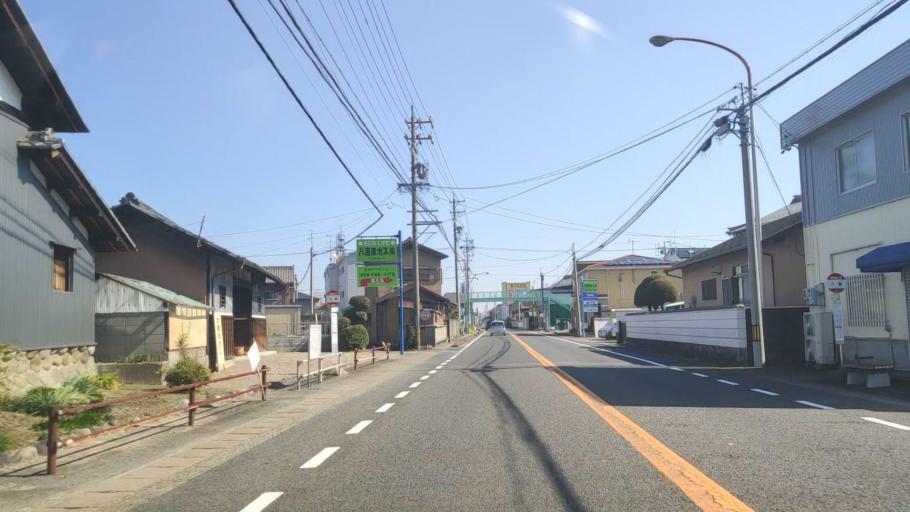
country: JP
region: Gifu
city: Kasamatsucho
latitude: 35.3946
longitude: 136.7785
